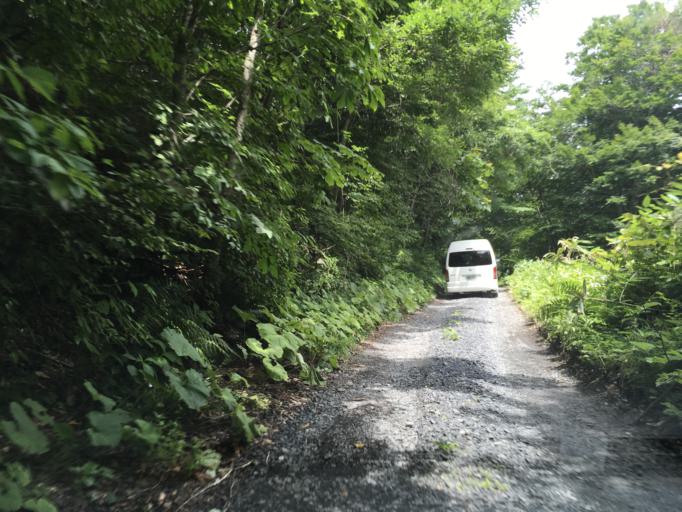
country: JP
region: Iwate
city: Ichinoseki
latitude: 38.9516
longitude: 140.8522
